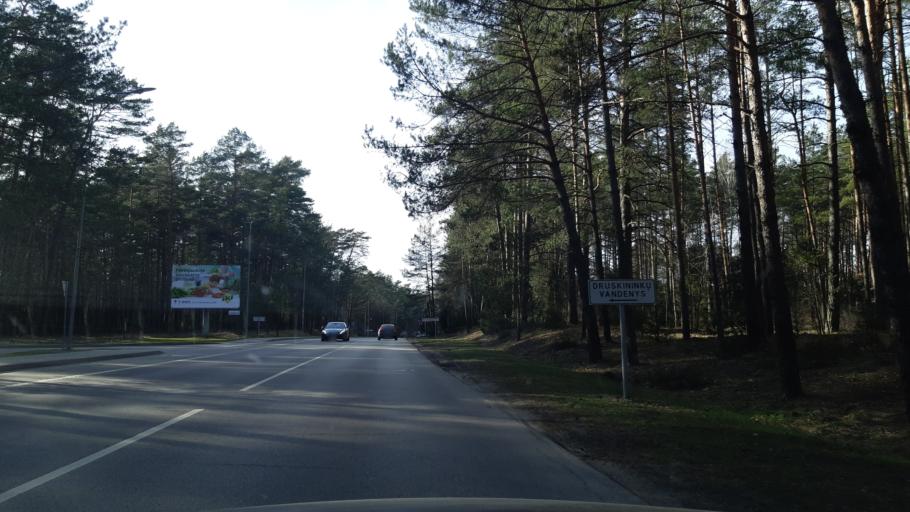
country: LT
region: Alytaus apskritis
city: Druskininkai
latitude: 54.0058
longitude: 24.0055
